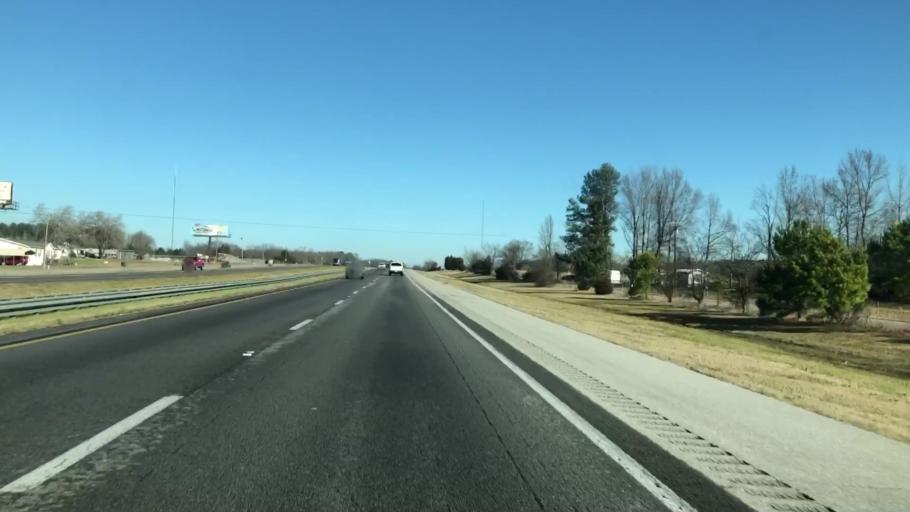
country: US
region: Alabama
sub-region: Limestone County
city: Athens
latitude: 34.8755
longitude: -86.9211
